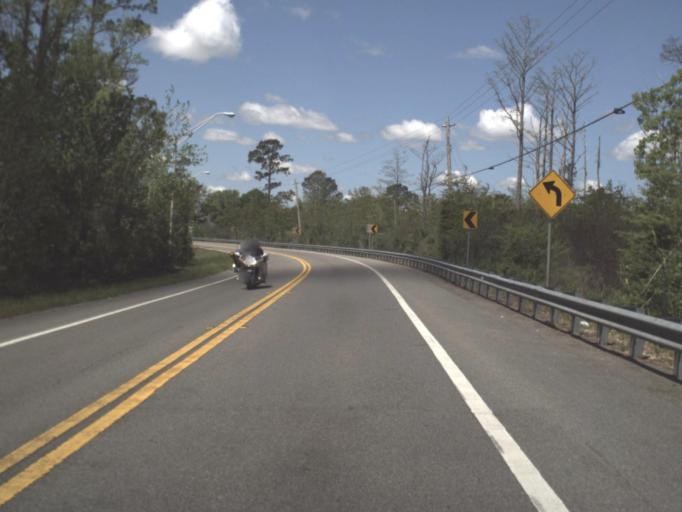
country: US
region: Florida
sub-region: Escambia County
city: Myrtle Grove
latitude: 30.4238
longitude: -87.3424
